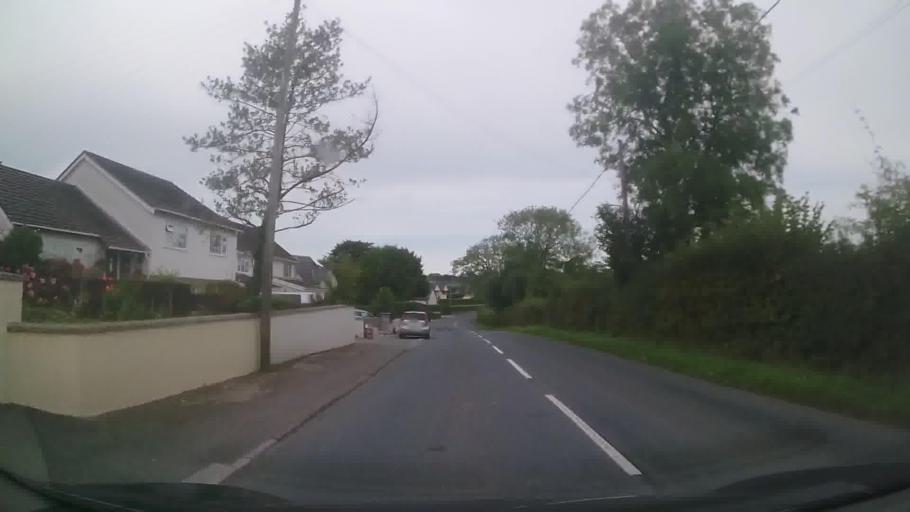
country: GB
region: Wales
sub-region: Pembrokeshire
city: Kilgetty
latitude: 51.7368
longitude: -4.7281
